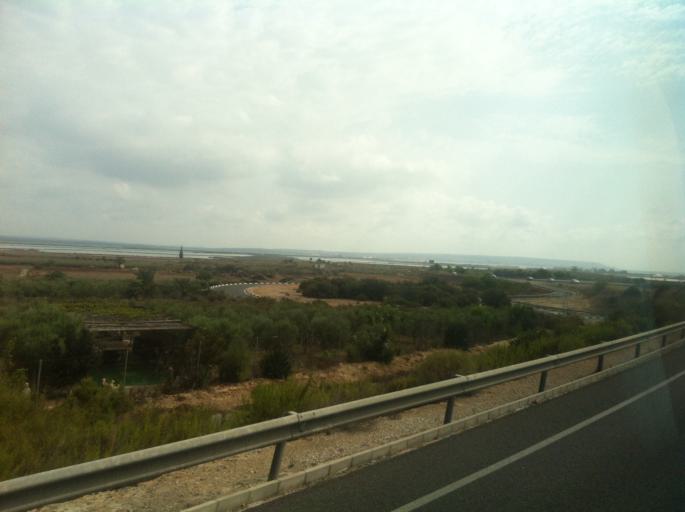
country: ES
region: Valencia
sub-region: Provincia de Alicante
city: Guardamar del Segura
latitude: 38.1609
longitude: -0.6378
